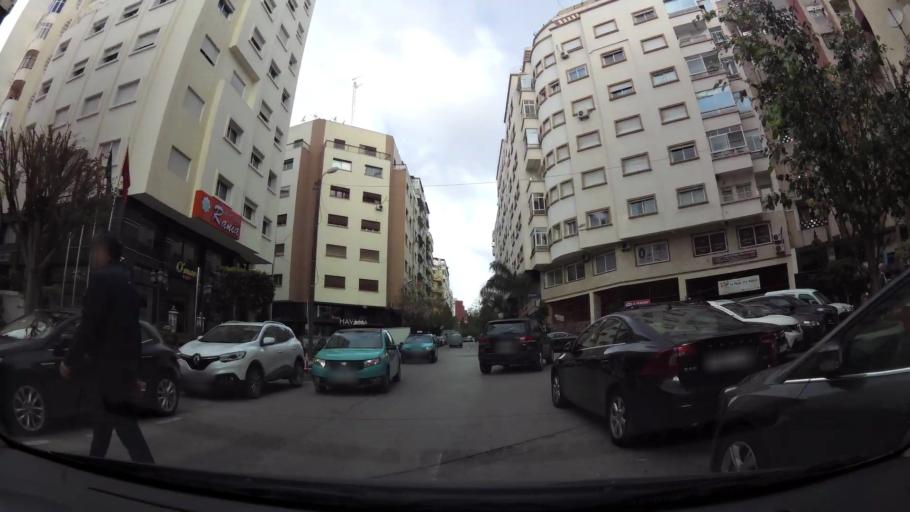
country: MA
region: Tanger-Tetouan
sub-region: Tanger-Assilah
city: Tangier
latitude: 35.7766
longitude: -5.8090
